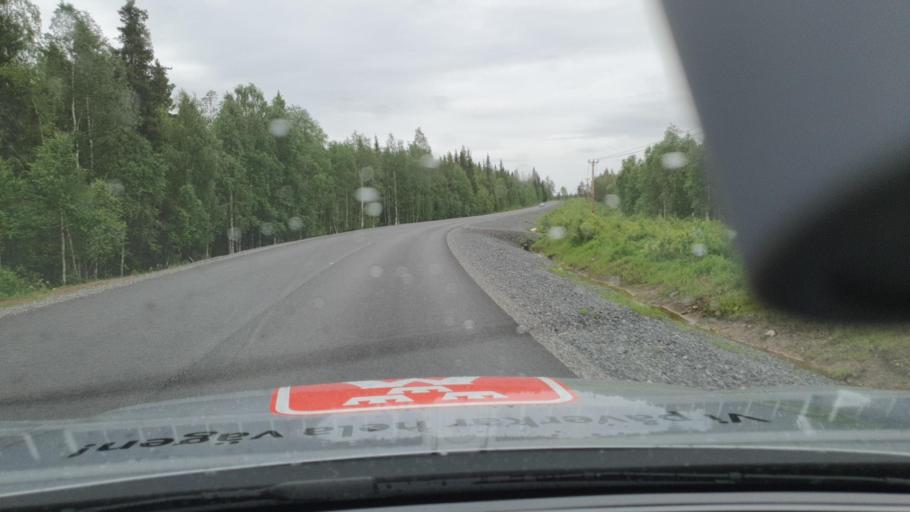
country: SE
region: Norrbotten
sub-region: Overkalix Kommun
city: OEverkalix
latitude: 66.7093
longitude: 23.2070
